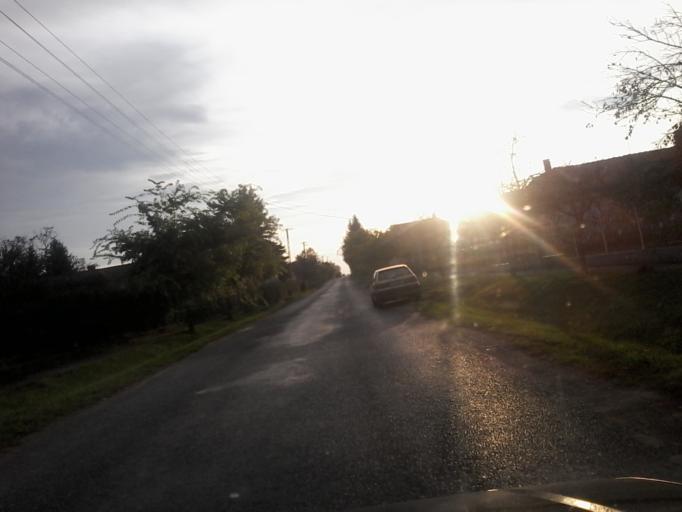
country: HU
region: Vas
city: Janoshaza
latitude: 47.1685
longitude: 17.1206
